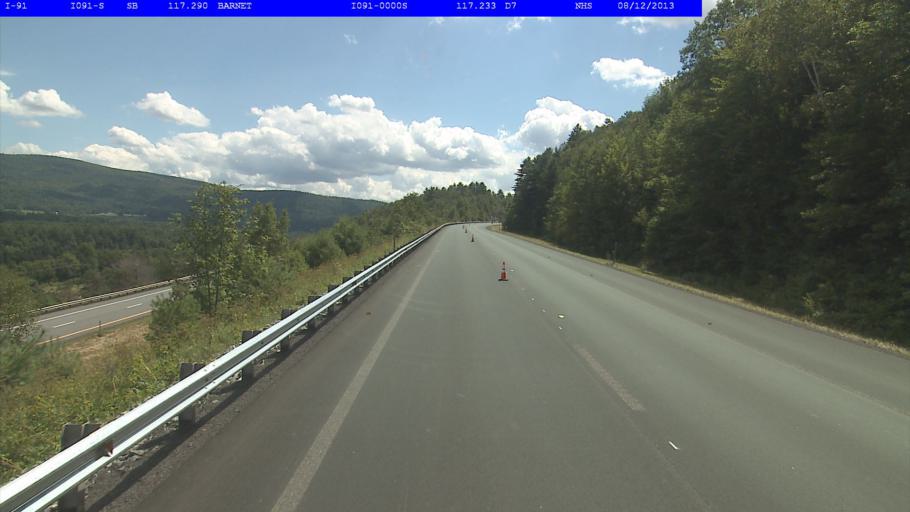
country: US
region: New Hampshire
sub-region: Grafton County
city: Woodsville
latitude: 44.2566
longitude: -72.0642
